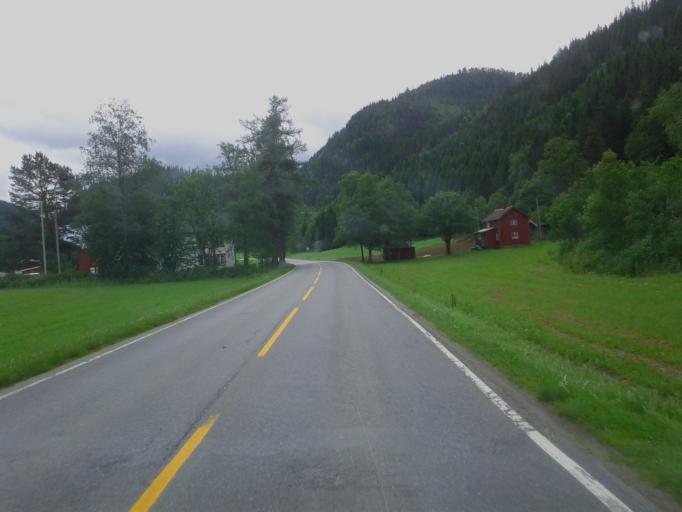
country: NO
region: Sor-Trondelag
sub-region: Midtre Gauldal
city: Storen
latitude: 62.9470
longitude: 10.6280
